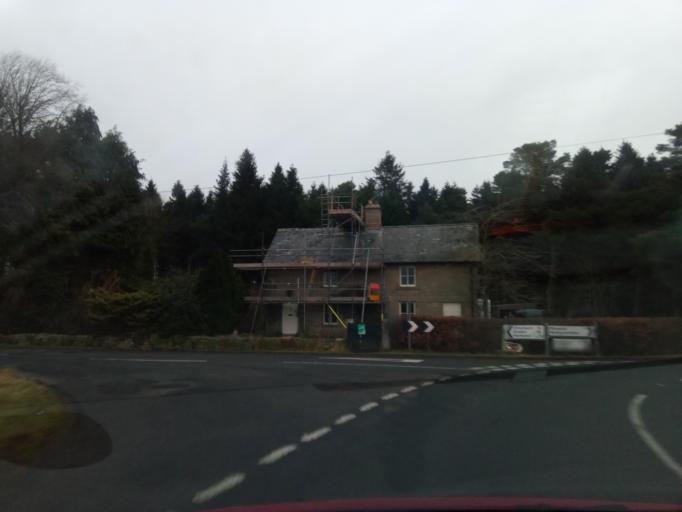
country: GB
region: England
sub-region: Northumberland
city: Rothley
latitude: 55.1987
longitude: -1.9729
